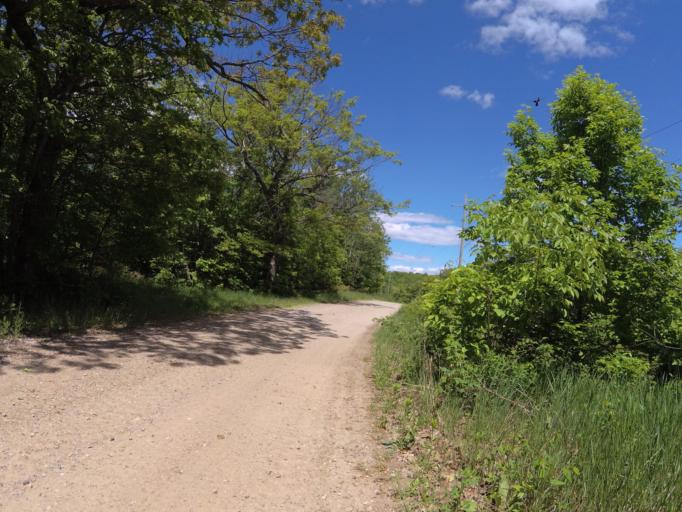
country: CA
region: Ontario
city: Renfrew
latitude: 45.0087
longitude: -76.9003
